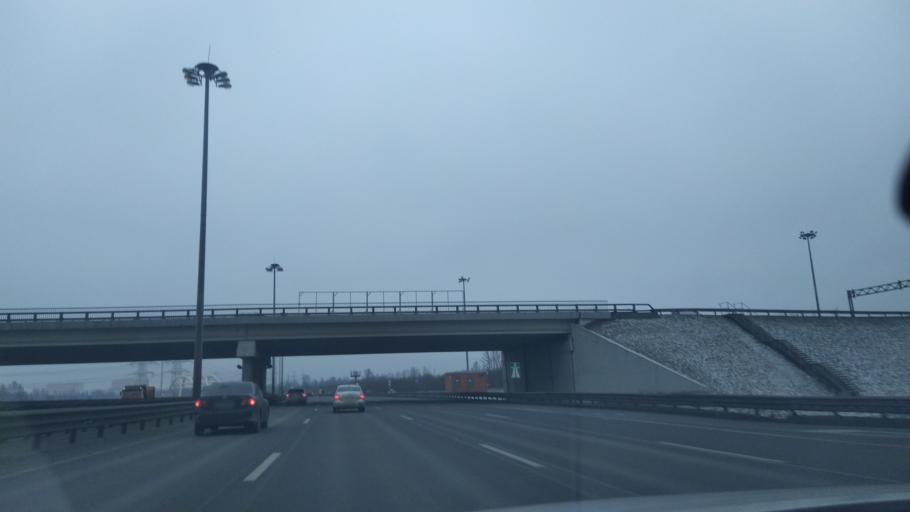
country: RU
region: St.-Petersburg
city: Krasnogvargeisky
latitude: 59.9909
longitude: 30.4824
